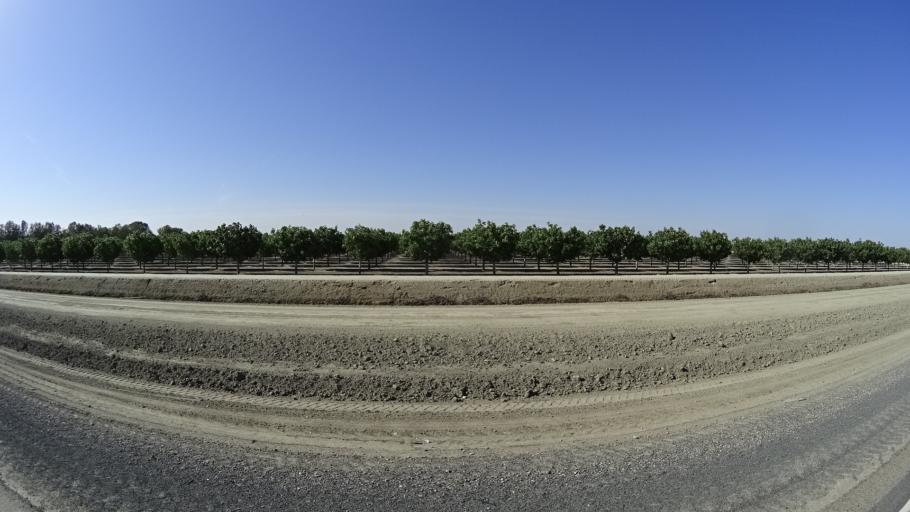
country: US
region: California
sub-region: Kings County
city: Corcoran
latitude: 36.0979
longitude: -119.5980
